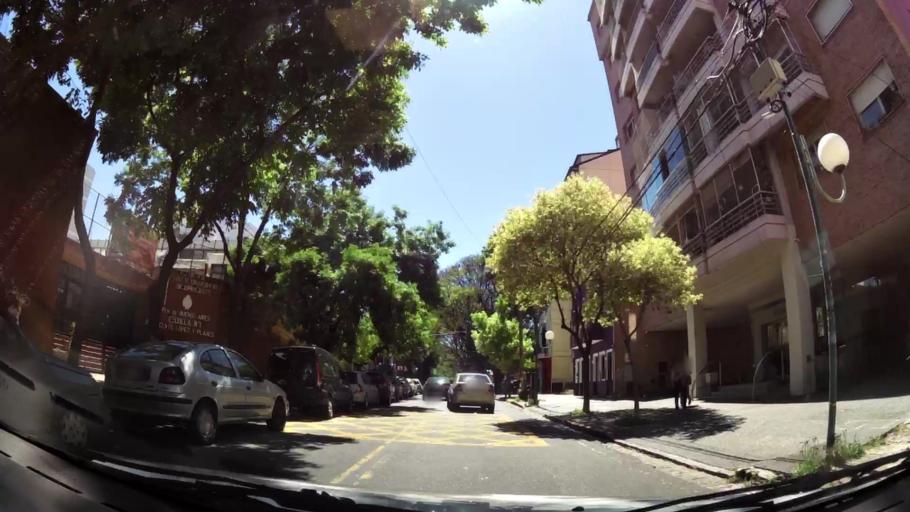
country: AR
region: Buenos Aires
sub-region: Partido de Vicente Lopez
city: Olivos
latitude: -34.5128
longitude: -58.4888
